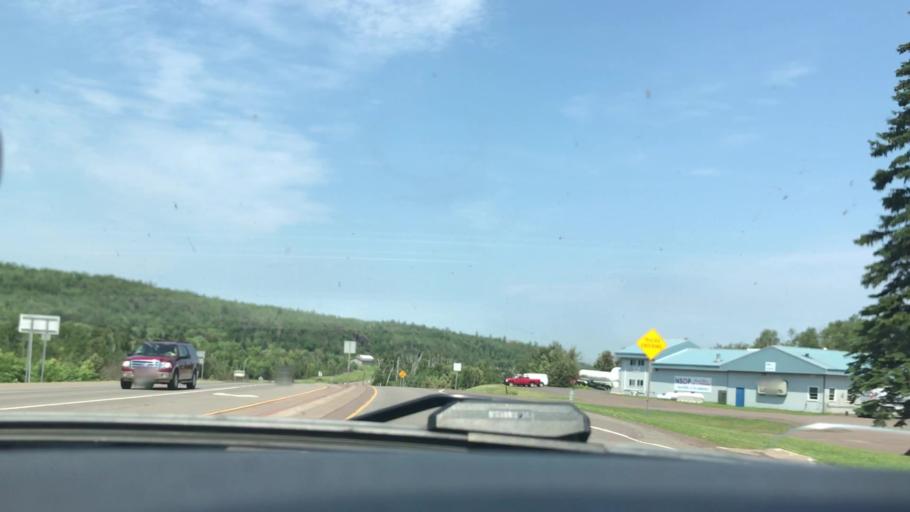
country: US
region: Minnesota
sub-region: Lake County
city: Silver Bay
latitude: 47.2947
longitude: -91.2571
